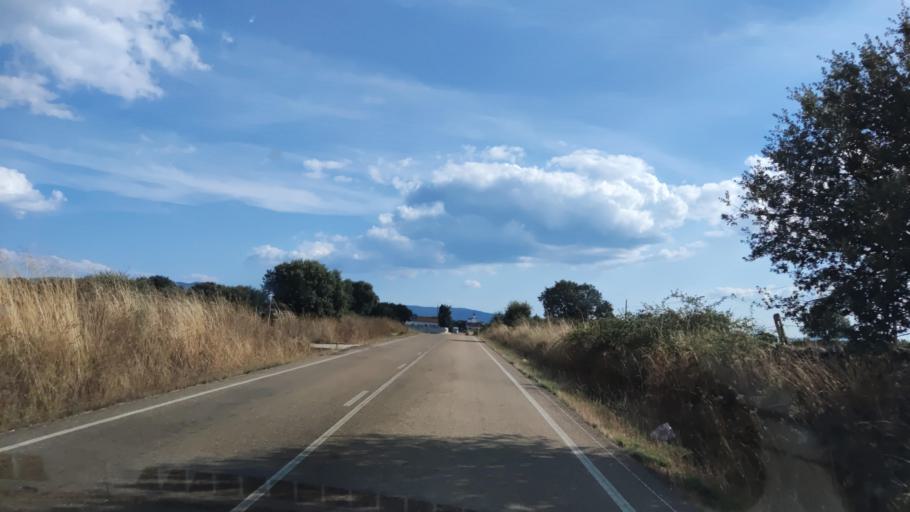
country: ES
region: Castille and Leon
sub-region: Provincia de Salamanca
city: Martiago
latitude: 40.4601
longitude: -6.4902
